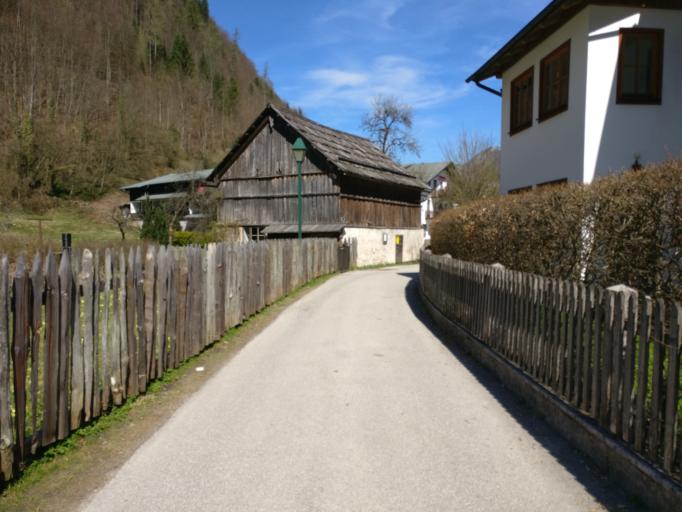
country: AT
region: Upper Austria
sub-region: Politischer Bezirk Gmunden
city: Bad Goisern
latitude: 47.5560
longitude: 13.6459
